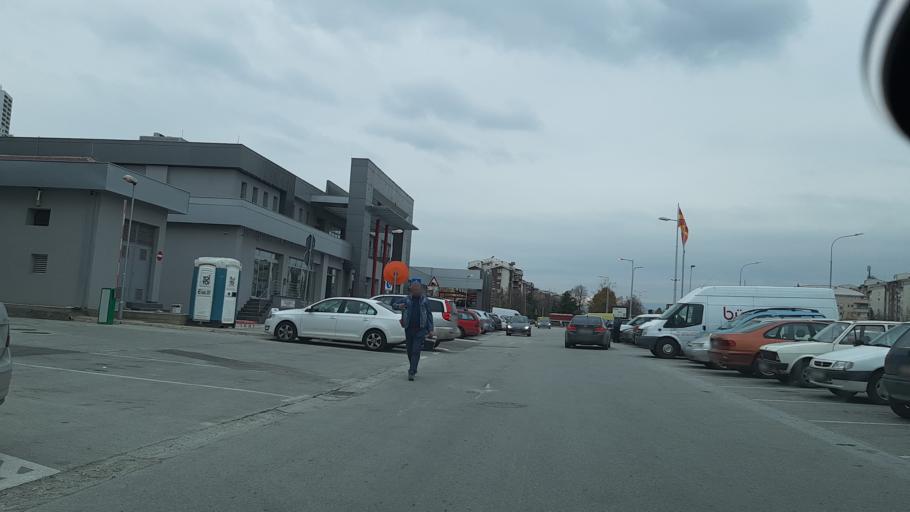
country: MK
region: Kisela Voda
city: Usje
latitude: 41.9814
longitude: 21.4730
